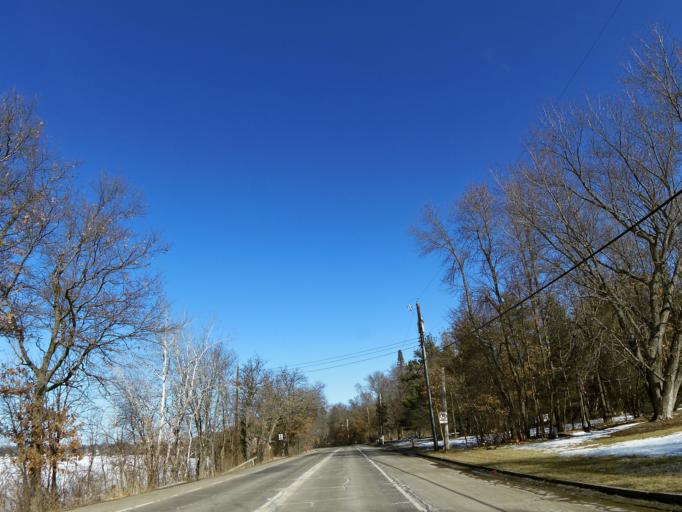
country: US
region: Minnesota
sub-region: Washington County
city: Lake Elmo
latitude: 44.9799
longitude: -92.8823
